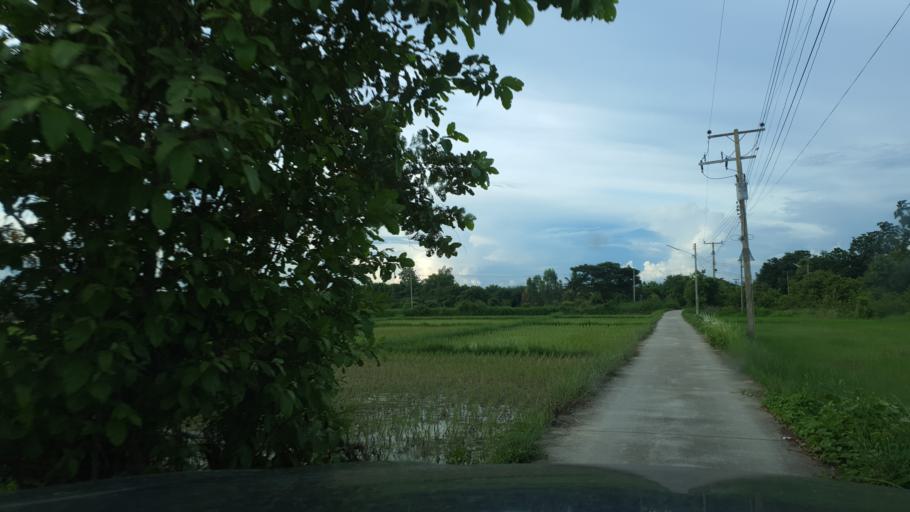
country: TH
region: Lamphun
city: Ban Thi
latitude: 18.6493
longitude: 99.1050
